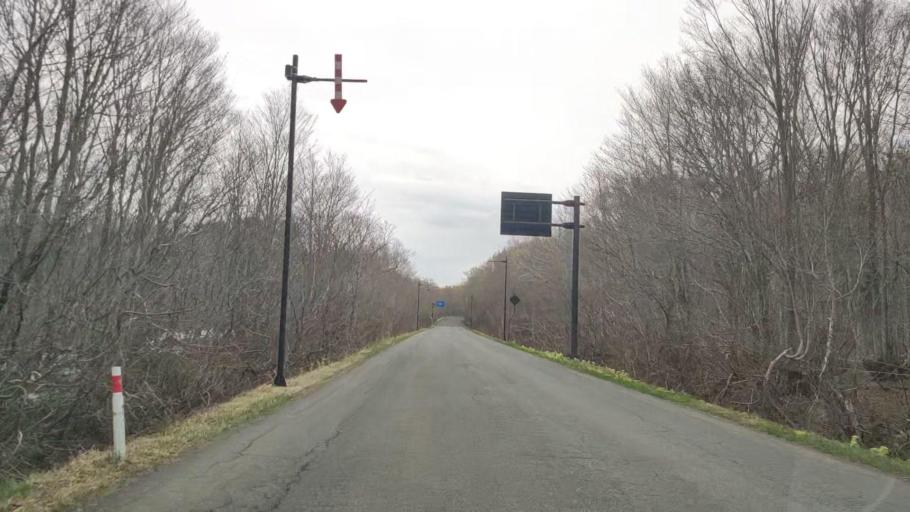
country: JP
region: Aomori
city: Aomori Shi
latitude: 40.6640
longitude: 140.9585
